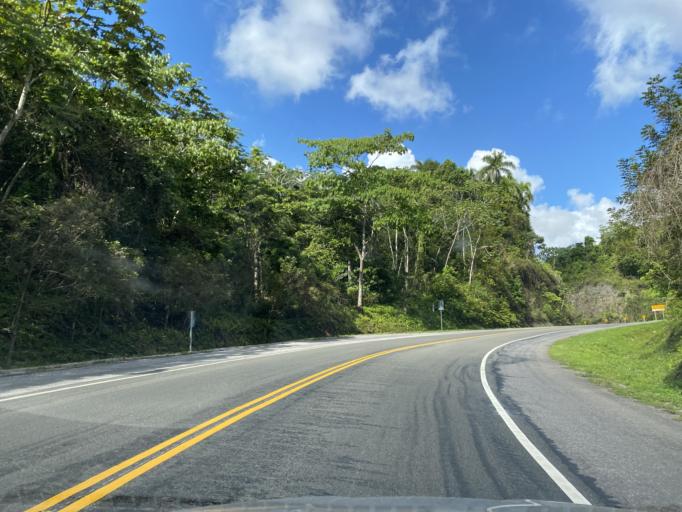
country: DO
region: Monte Plata
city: Majagual
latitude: 19.0800
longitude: -69.8288
